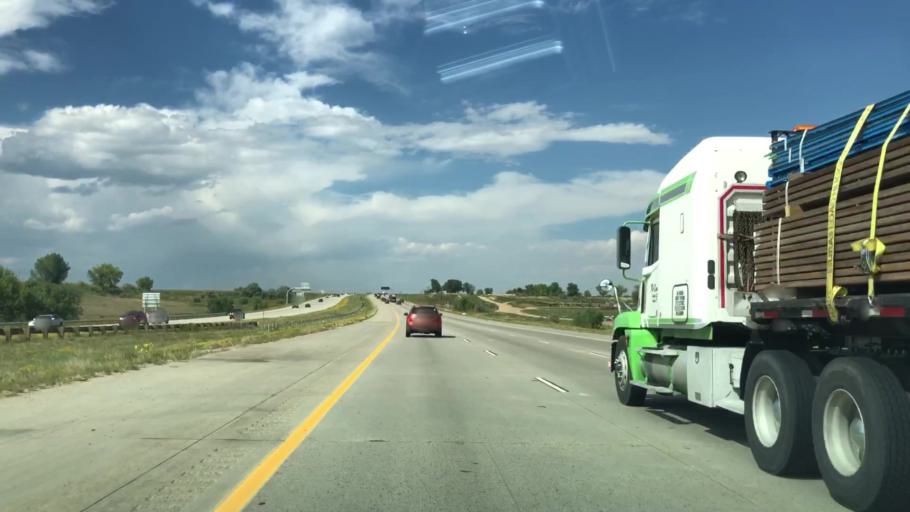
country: US
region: Colorado
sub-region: Weld County
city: Mead
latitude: 40.1769
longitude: -104.9790
